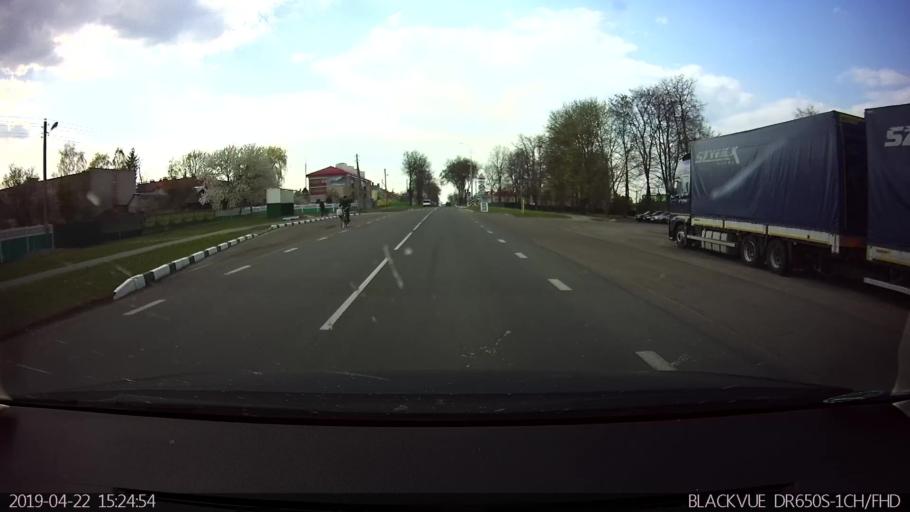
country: BY
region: Brest
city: Vysokaye
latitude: 52.3627
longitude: 23.4017
